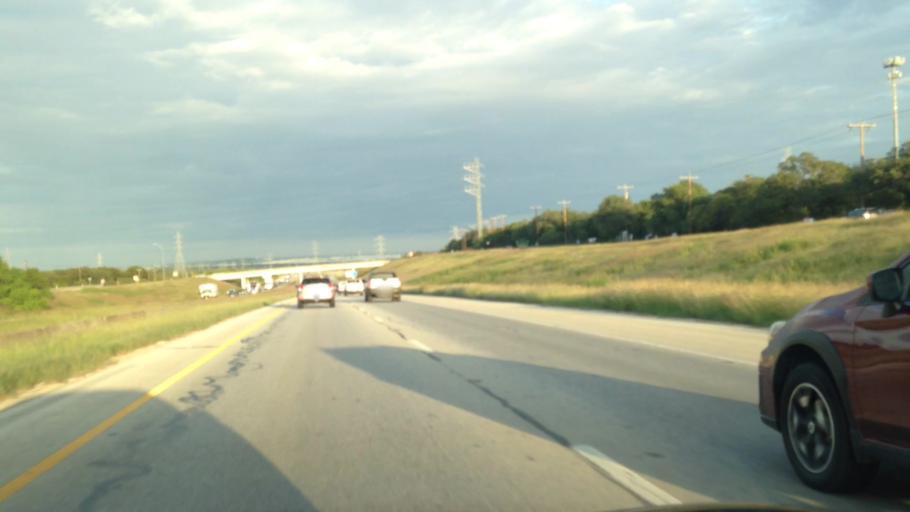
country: US
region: Texas
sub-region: Bexar County
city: Live Oak
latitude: 29.6026
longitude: -98.3705
